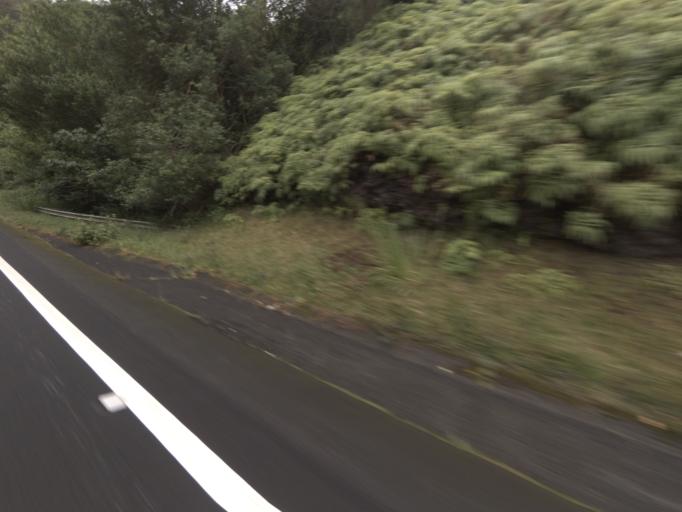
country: US
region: Hawaii
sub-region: Honolulu County
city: Kane'ohe
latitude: 21.3855
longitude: -157.8152
